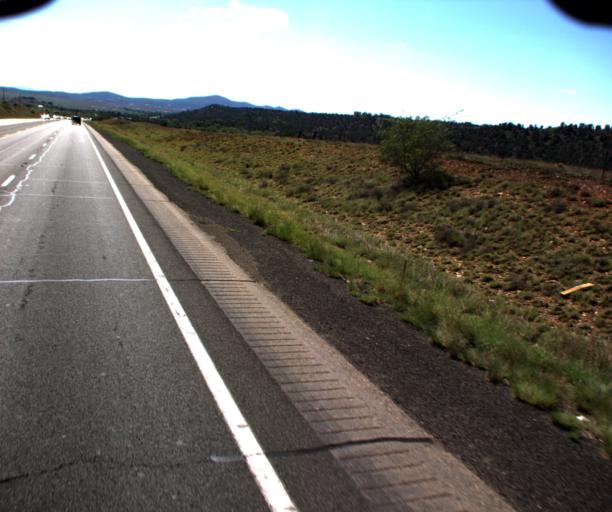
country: US
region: Arizona
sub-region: Yavapai County
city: Prescott Valley
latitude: 34.5762
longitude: -112.2880
